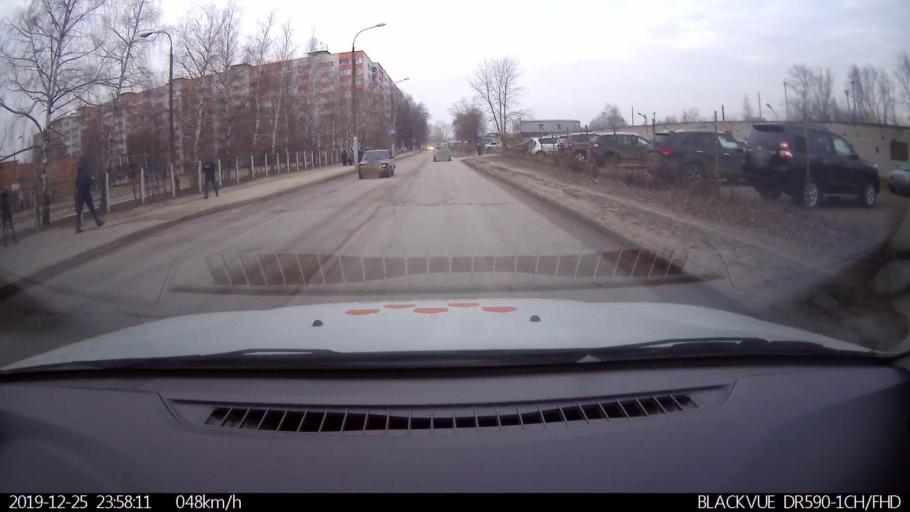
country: RU
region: Nizjnij Novgorod
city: Gorbatovka
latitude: 56.2625
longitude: 43.8624
